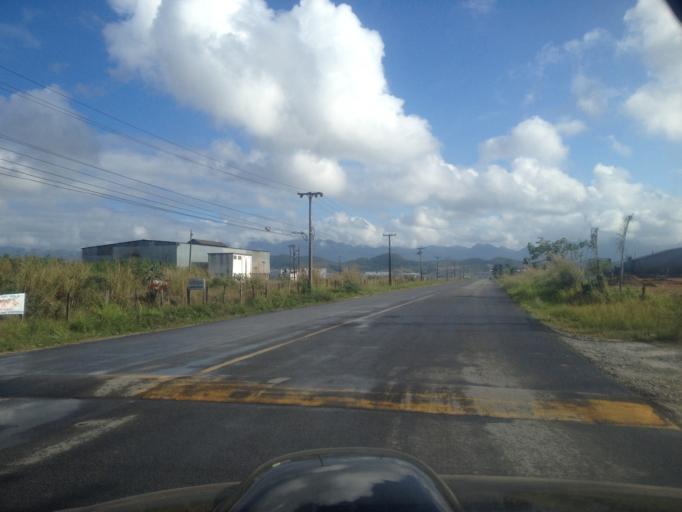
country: BR
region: Rio de Janeiro
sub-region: Resende
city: Resende
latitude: -22.4506
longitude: -44.3762
